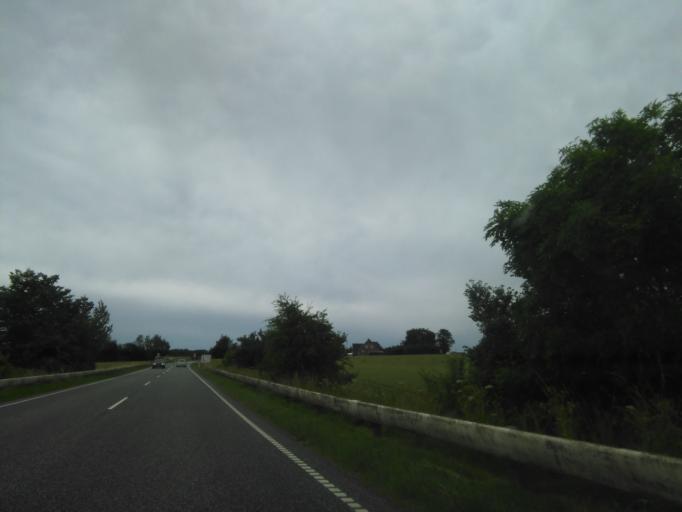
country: DK
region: Central Jutland
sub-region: Skanderborg Kommune
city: Stilling
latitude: 55.9616
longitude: 9.9928
